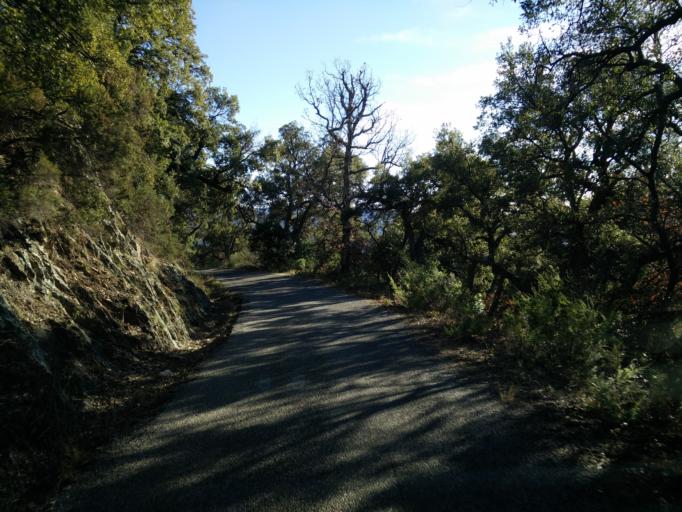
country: FR
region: Provence-Alpes-Cote d'Azur
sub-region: Departement du Var
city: Collobrieres
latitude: 43.2761
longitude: 6.2971
